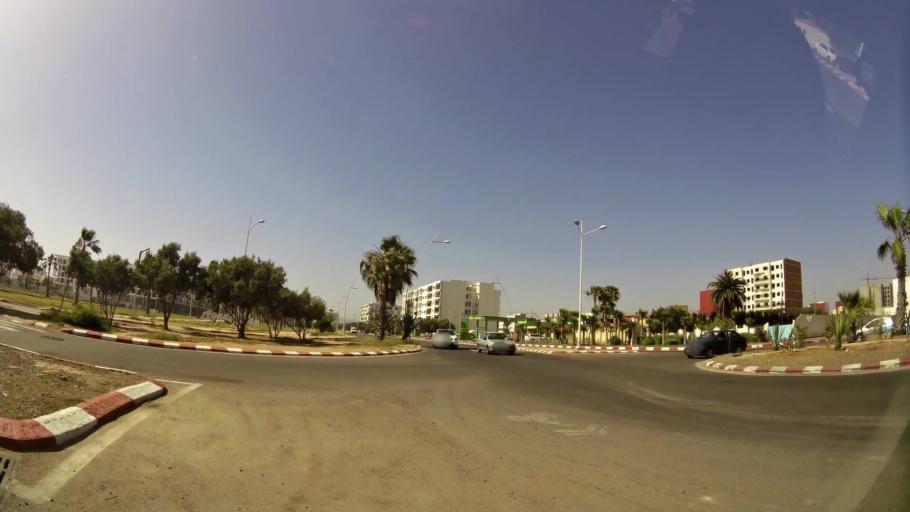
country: MA
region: Souss-Massa-Draa
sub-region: Agadir-Ida-ou-Tnan
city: Agadir
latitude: 30.3976
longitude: -9.5815
